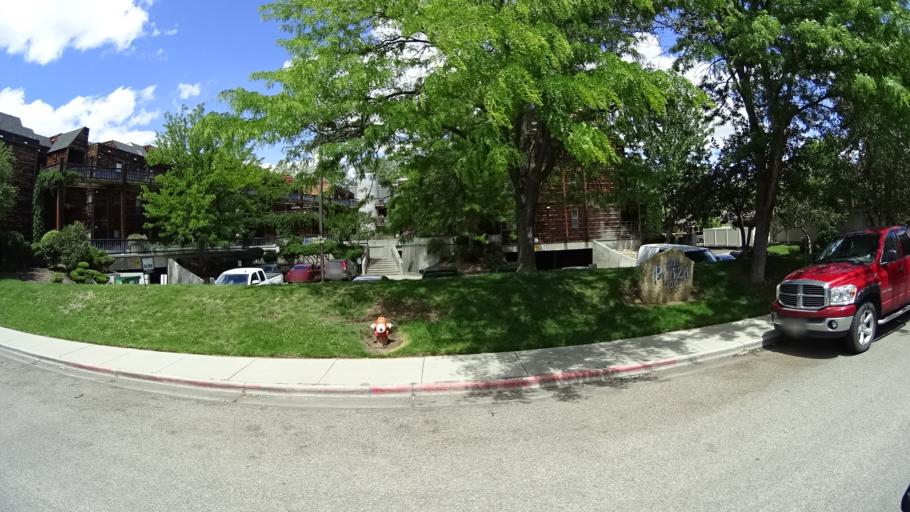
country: US
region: Idaho
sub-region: Ada County
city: Boise
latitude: 43.5958
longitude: -116.1829
